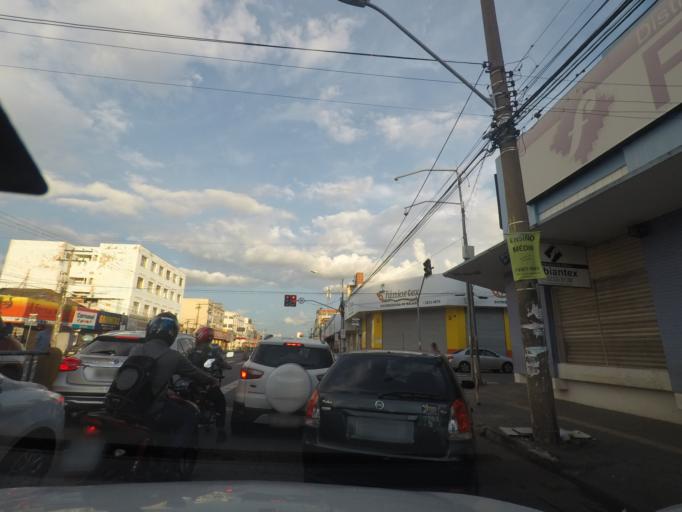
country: BR
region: Goias
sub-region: Goiania
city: Goiania
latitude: -16.6729
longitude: -49.2881
